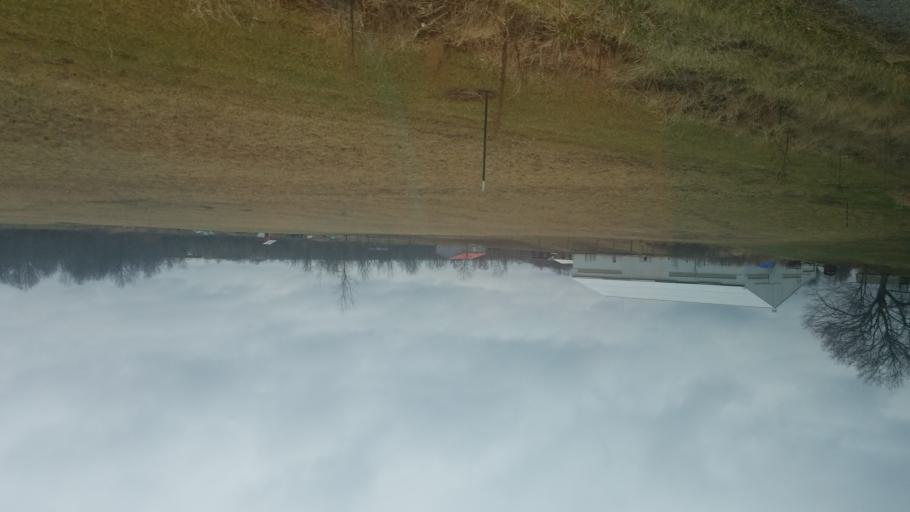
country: US
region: Ohio
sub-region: Crawford County
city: Galion
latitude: 40.7570
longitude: -82.7601
